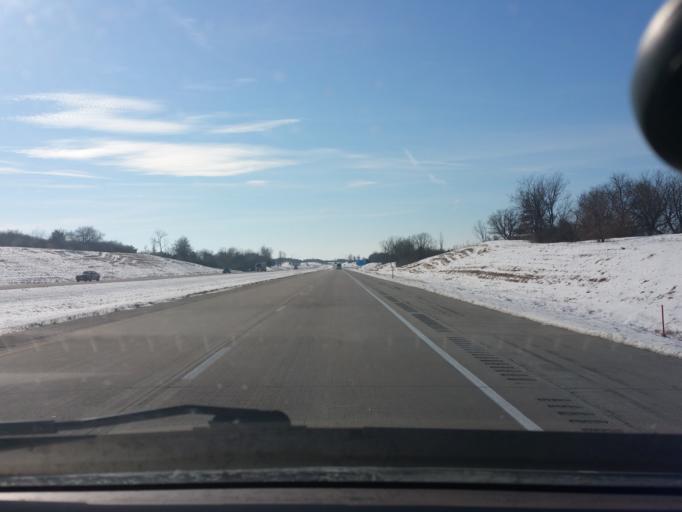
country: US
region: Iowa
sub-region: Decatur County
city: Leon
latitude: 40.7510
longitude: -93.8392
